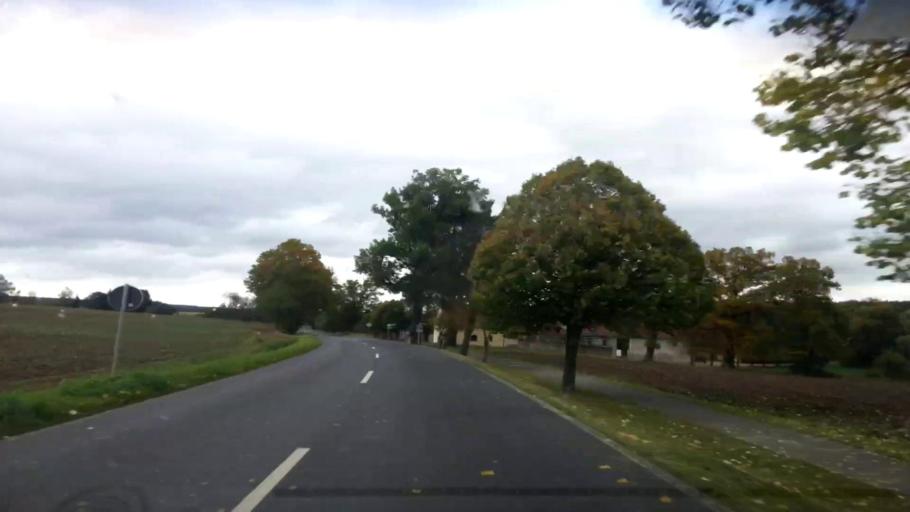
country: DE
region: Bavaria
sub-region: Upper Palatinate
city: Waldsassen
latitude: 50.0126
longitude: 12.3177
